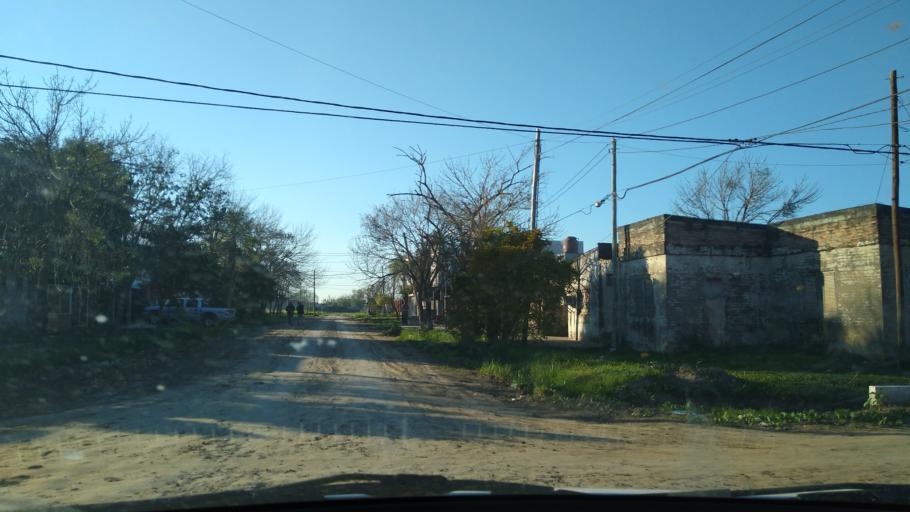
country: AR
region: Chaco
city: Resistencia
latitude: -27.4838
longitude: -58.9675
